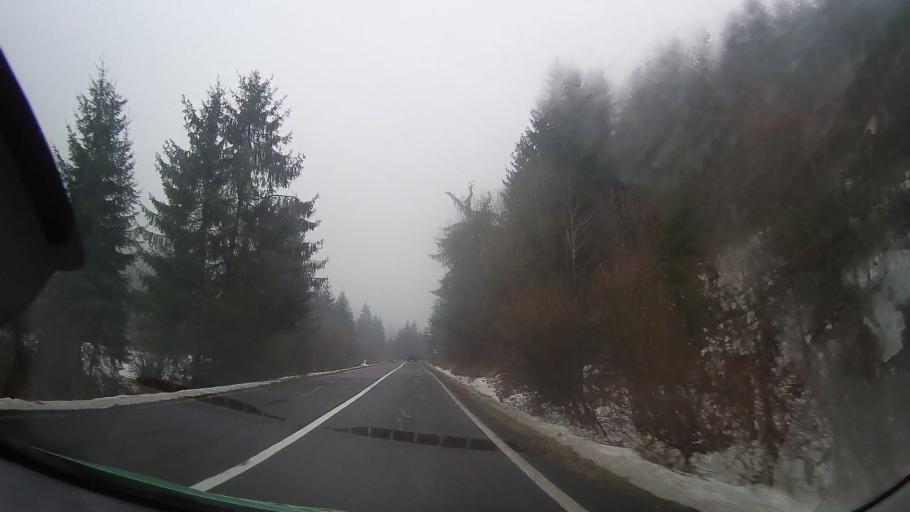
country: RO
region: Harghita
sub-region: Municipiul Gheorgheni
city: Gheorgheni
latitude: 46.7531
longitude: 25.6908
